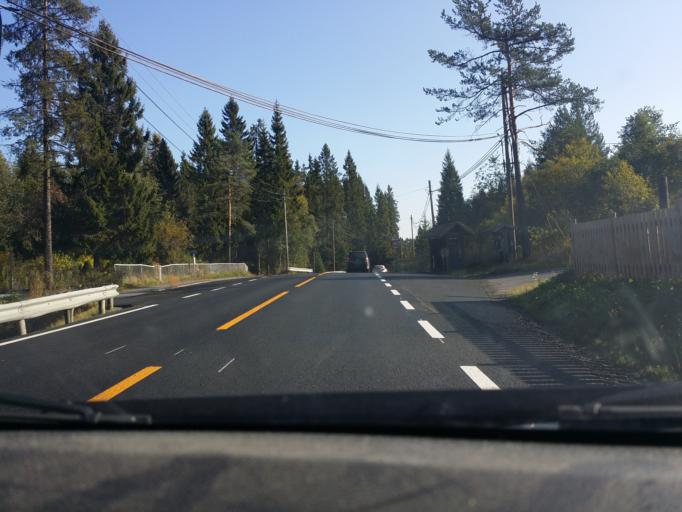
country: NO
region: Akershus
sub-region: Baerum
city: Skui
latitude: 59.9570
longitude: 10.3701
